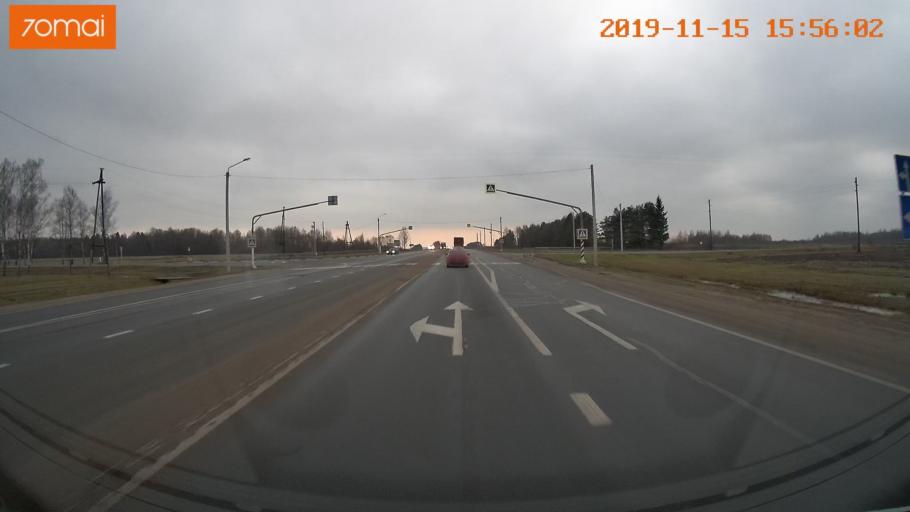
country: RU
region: Jaroslavl
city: Yaroslavl
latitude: 57.8463
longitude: 39.9775
